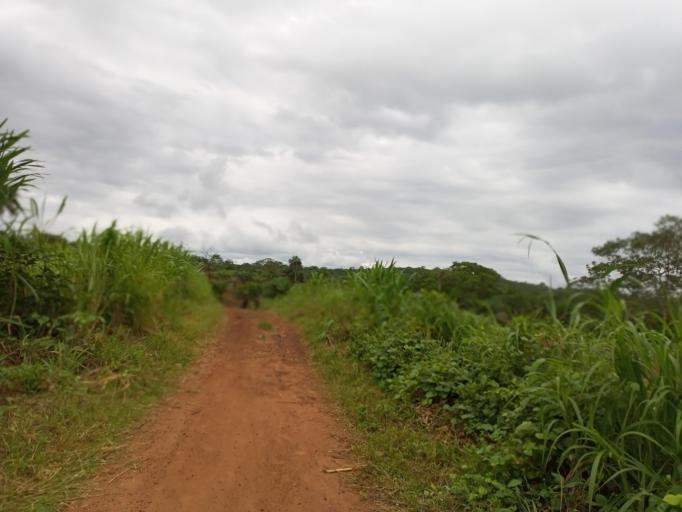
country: SL
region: Northern Province
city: Kamakwie
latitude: 9.5051
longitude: -12.2667
